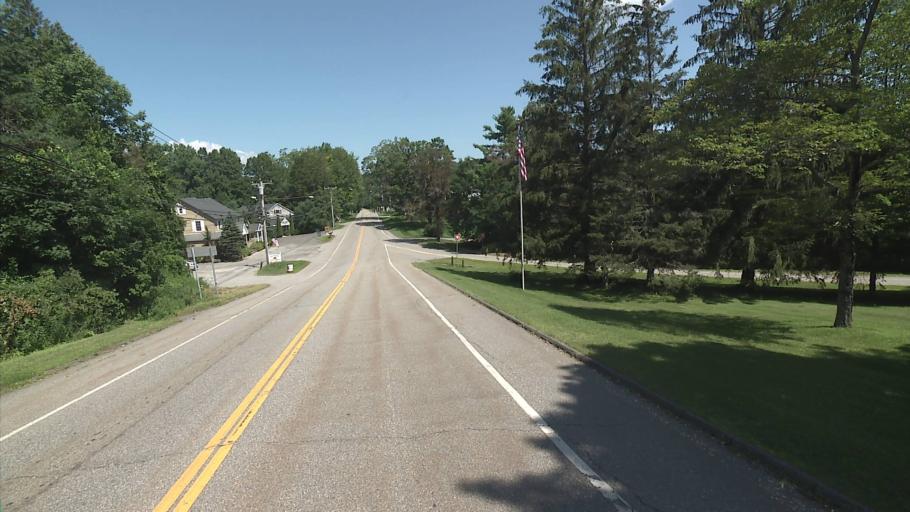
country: US
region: Connecticut
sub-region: Litchfield County
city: New Preston
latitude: 41.7447
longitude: -73.3489
